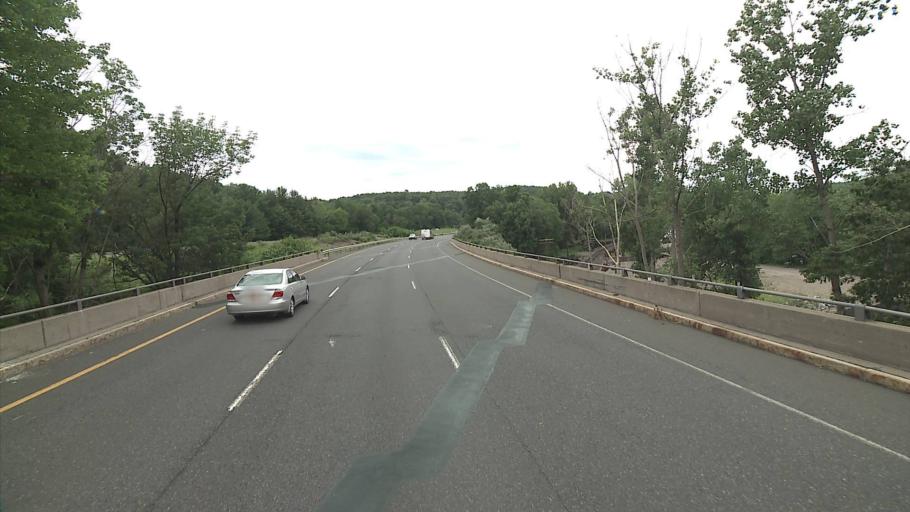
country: US
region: Connecticut
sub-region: Litchfield County
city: Thomaston
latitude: 41.6790
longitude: -73.0648
